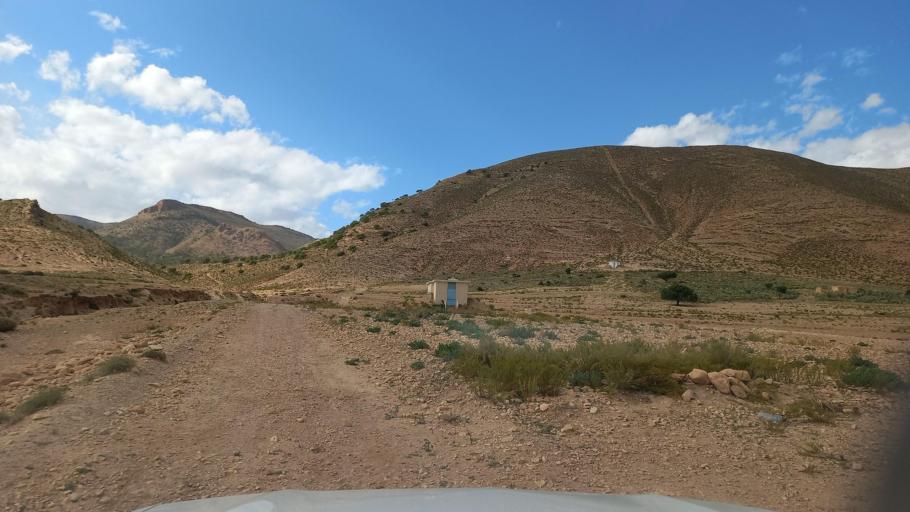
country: TN
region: Al Qasrayn
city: Sbiba
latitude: 35.4533
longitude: 9.0614
